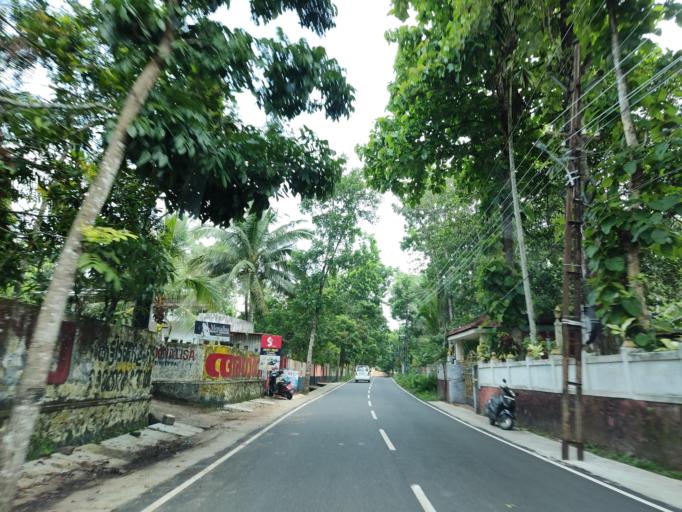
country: IN
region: Kerala
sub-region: Alappuzha
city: Mavelikara
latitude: 9.2653
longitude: 76.5593
